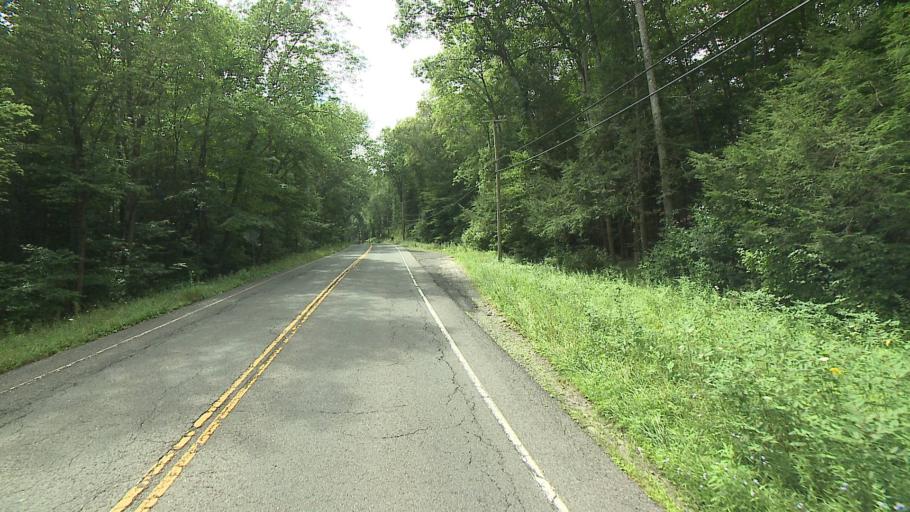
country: US
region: Connecticut
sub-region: Fairfield County
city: Sherman
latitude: 41.6448
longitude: -73.5029
